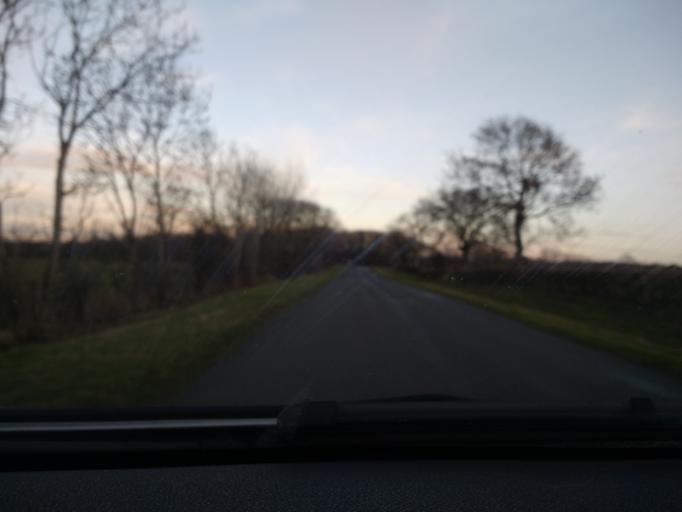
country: GB
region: England
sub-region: Cumbria
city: Carlisle
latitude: 54.7325
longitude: -2.9381
